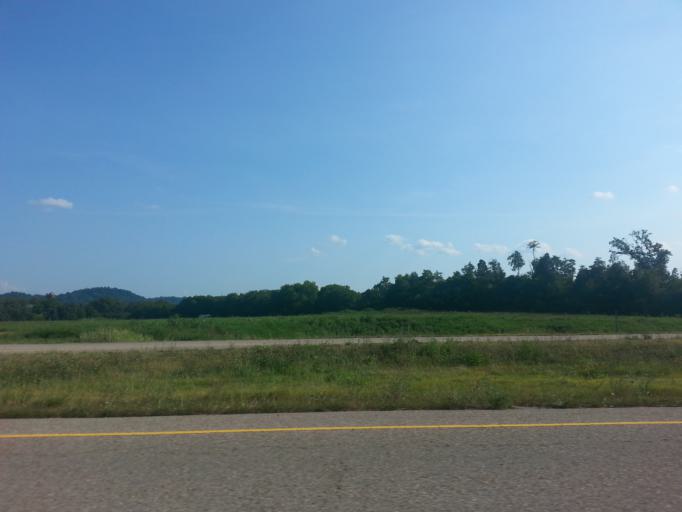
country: US
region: Tennessee
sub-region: Loudon County
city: Greenback
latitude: 35.7375
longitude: -84.1873
